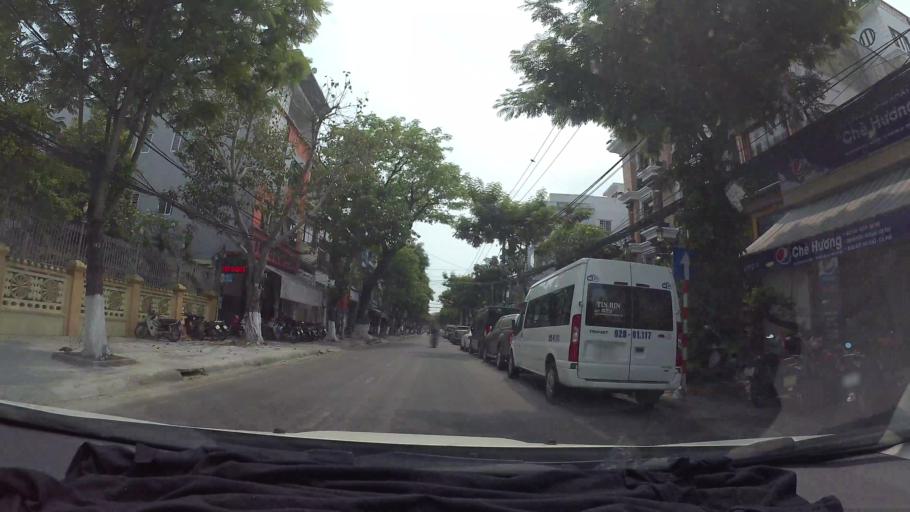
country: VN
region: Da Nang
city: Da Nang
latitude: 16.0583
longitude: 108.2191
